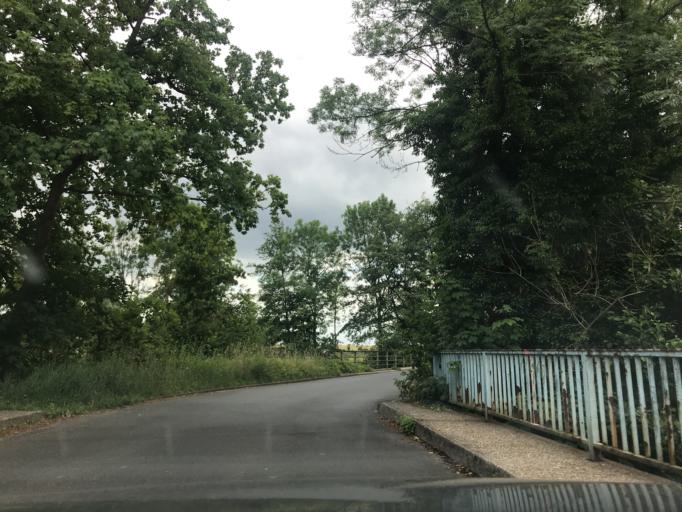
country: DE
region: North Rhine-Westphalia
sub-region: Regierungsbezirk Dusseldorf
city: Neuss
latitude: 51.1540
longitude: 6.6794
